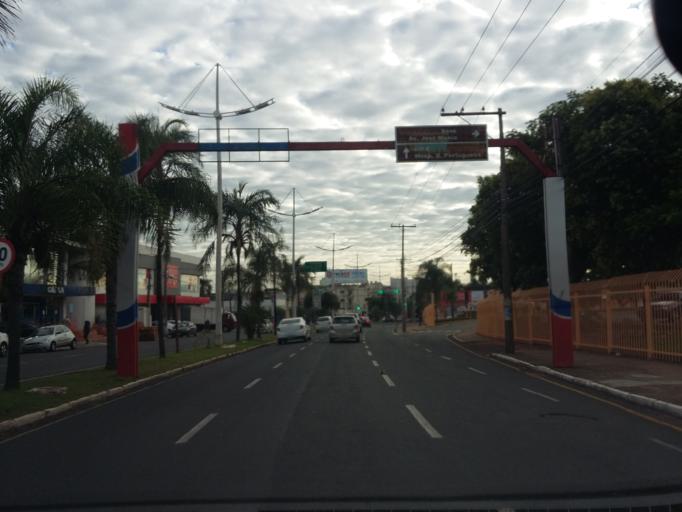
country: BR
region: Sao Paulo
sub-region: Sao Jose Do Rio Preto
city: Sao Jose do Rio Preto
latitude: -20.8342
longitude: -49.3999
